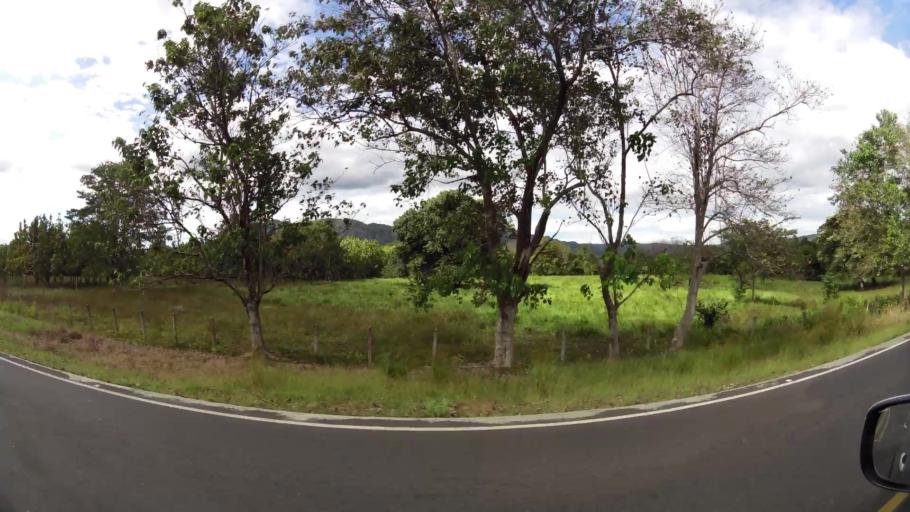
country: CR
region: Guanacaste
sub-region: Canton de Nicoya
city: Nicoya
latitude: 10.1409
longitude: -85.3331
